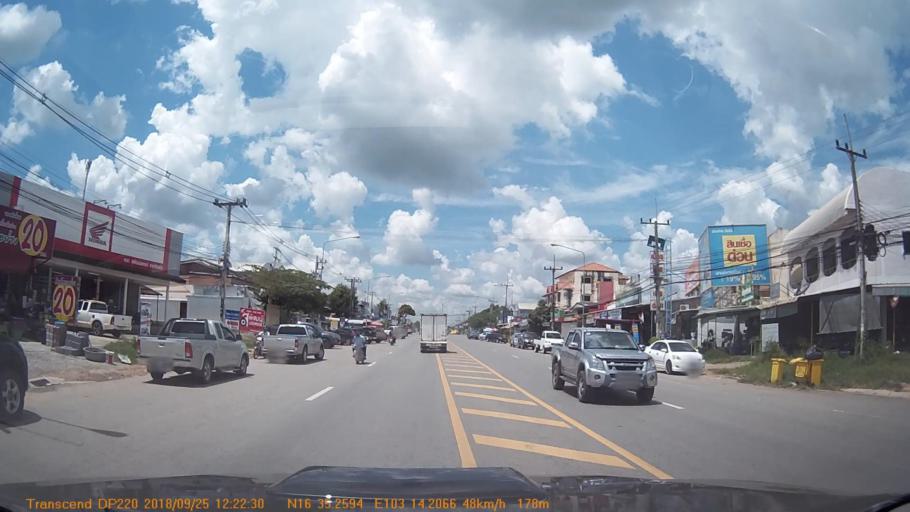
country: TH
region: Kalasin
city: Huai Mek
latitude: 16.5876
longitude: 103.2369
